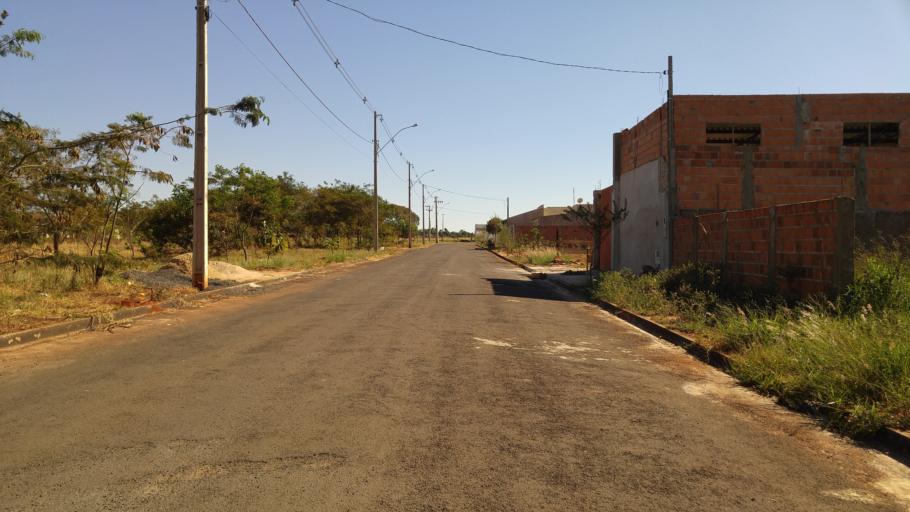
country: BR
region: Sao Paulo
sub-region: Paraguacu Paulista
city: Paraguacu Paulista
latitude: -22.4411
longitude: -50.5881
